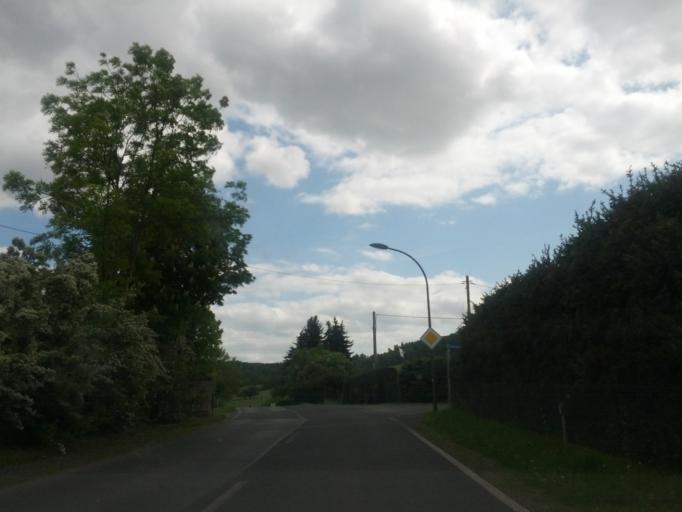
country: DE
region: Saxony
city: Kreischa
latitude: 50.9402
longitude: 13.7674
